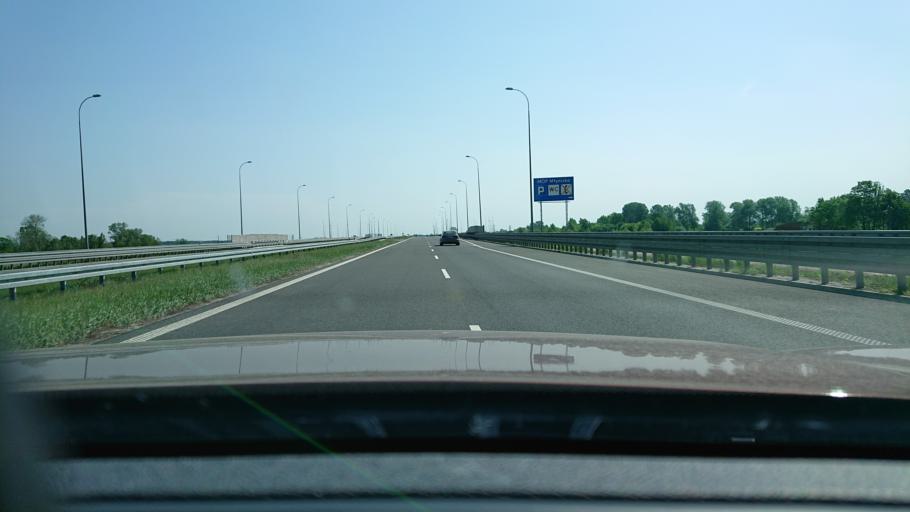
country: PL
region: Subcarpathian Voivodeship
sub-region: Powiat lancucki
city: Rogozno
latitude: 50.1115
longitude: 22.3994
